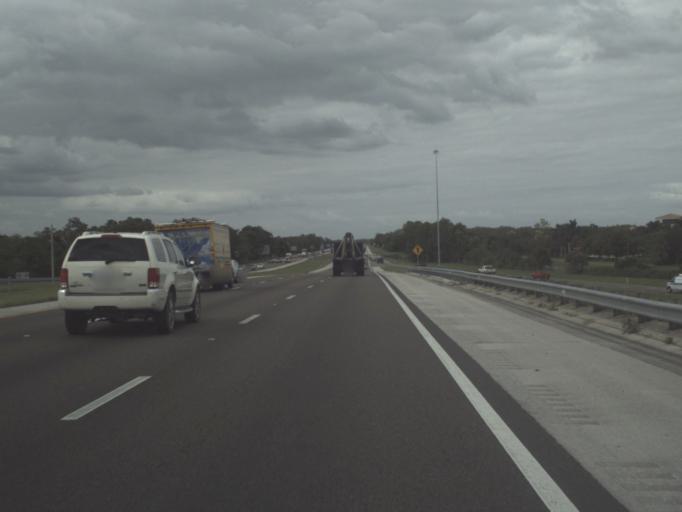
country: US
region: Florida
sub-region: Collier County
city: Vineyards
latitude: 26.2737
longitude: -81.7425
